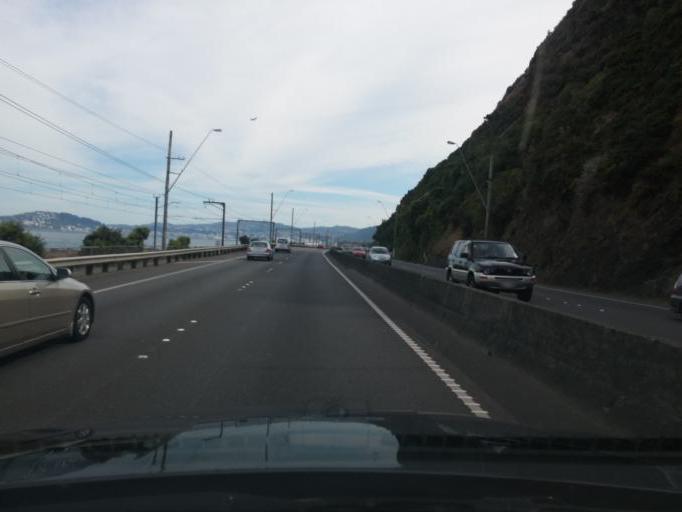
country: NZ
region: Wellington
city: Petone
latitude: -41.2390
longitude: 174.8276
